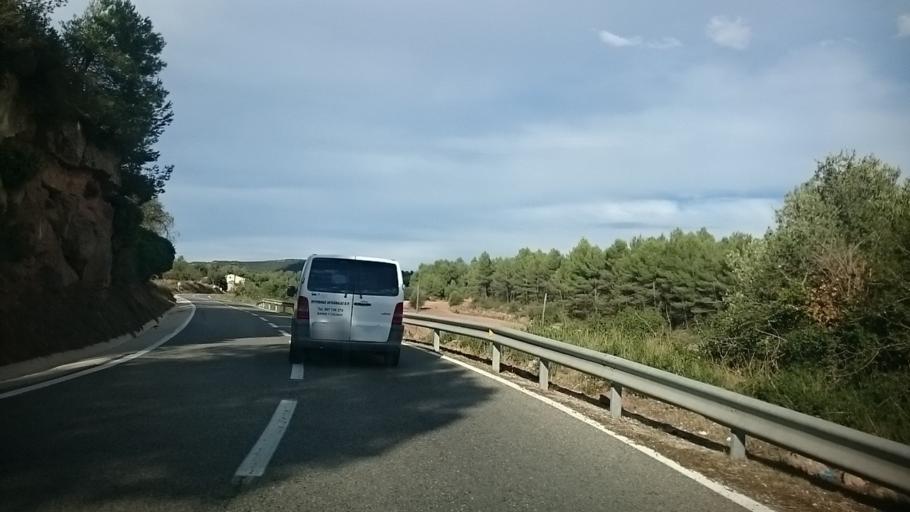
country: ES
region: Catalonia
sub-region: Provincia de Barcelona
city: Odena
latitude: 41.6220
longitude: 1.6562
